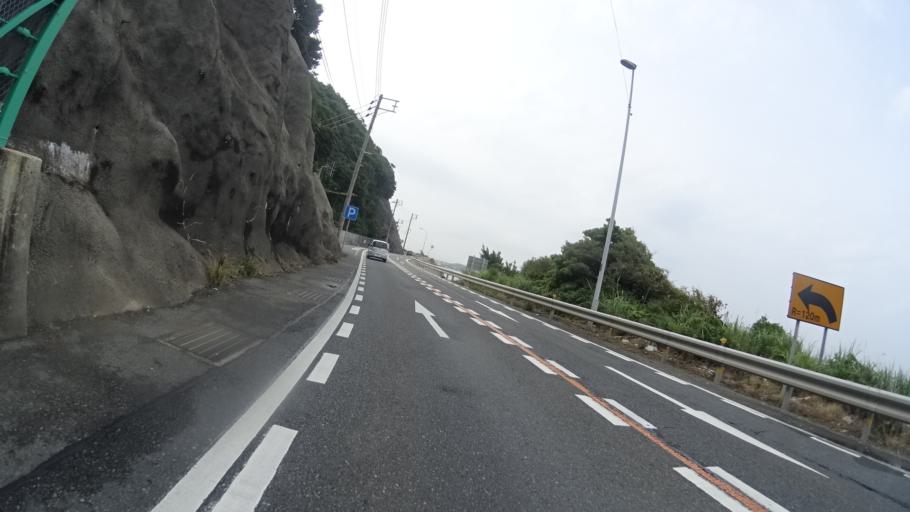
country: JP
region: Yamaguchi
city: Shimonoseki
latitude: 34.0557
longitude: 130.9120
